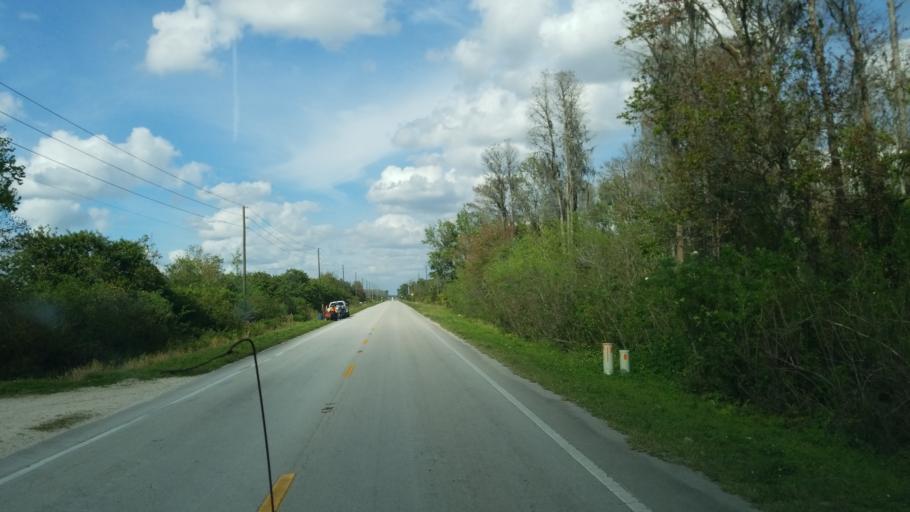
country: US
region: Florida
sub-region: Osceola County
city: Saint Cloud
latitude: 28.1188
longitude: -81.0763
